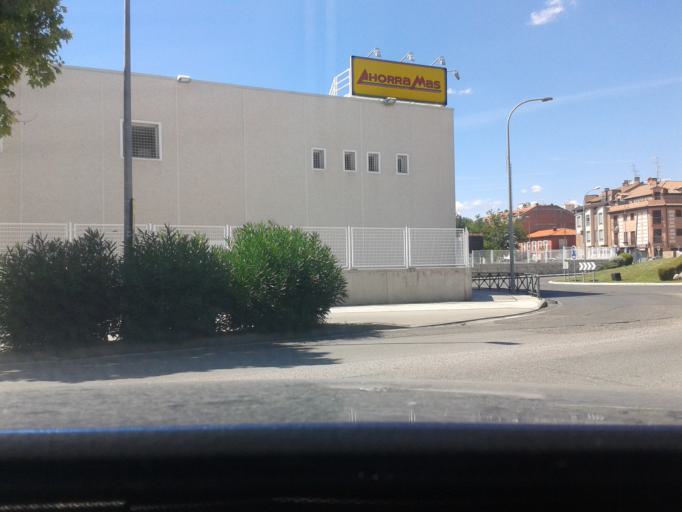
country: ES
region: Castille-La Mancha
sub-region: Provincia de Guadalajara
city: Alovera
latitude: 40.5935
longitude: -3.2514
